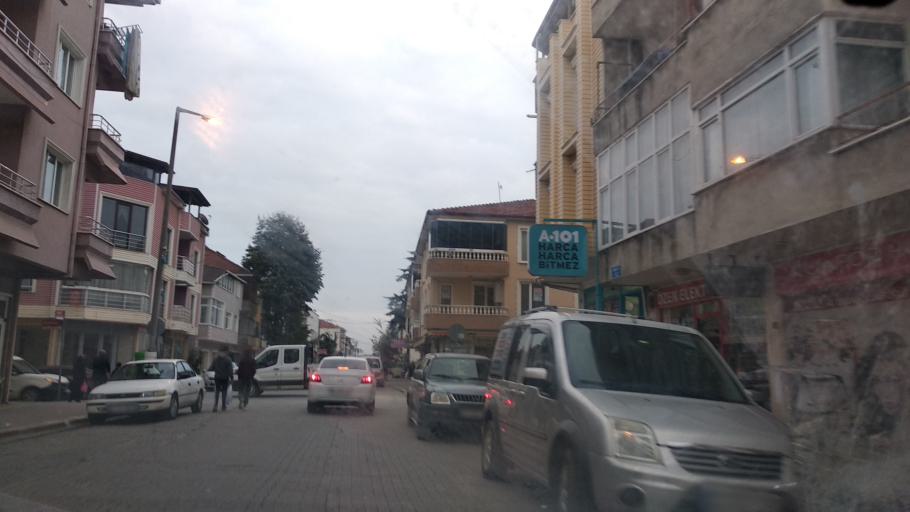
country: TR
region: Sakarya
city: Karasu
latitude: 41.0934
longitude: 30.6941
